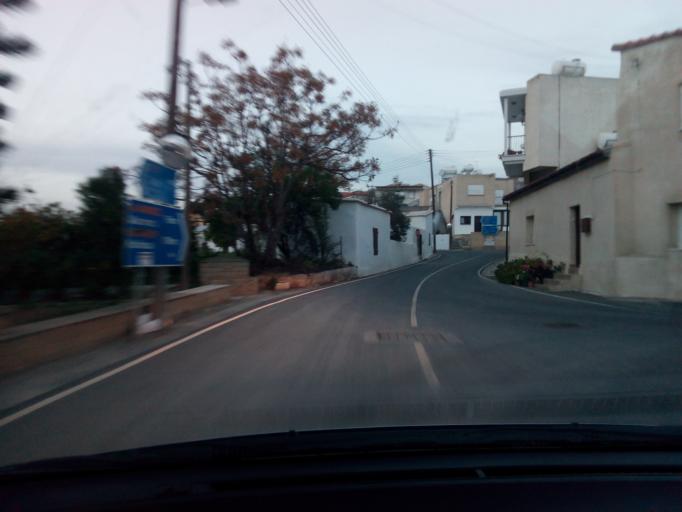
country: CY
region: Larnaka
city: Tersefanou
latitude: 34.8034
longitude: 33.4869
